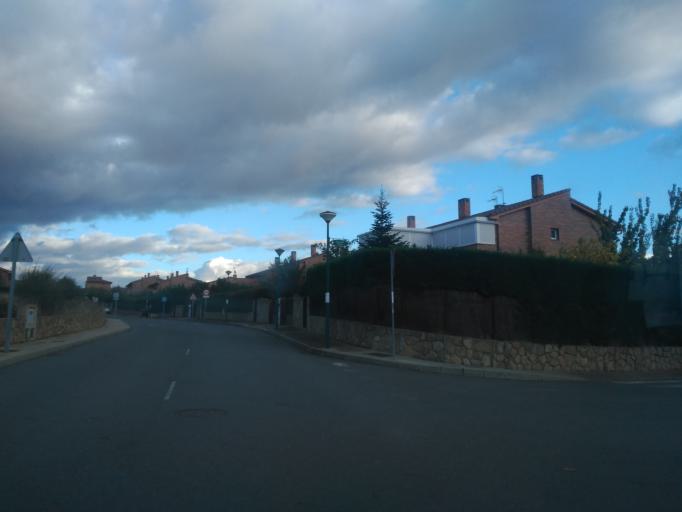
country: ES
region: Castille and Leon
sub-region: Provincia de Salamanca
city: Villamayor
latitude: 40.9825
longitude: -5.7073
